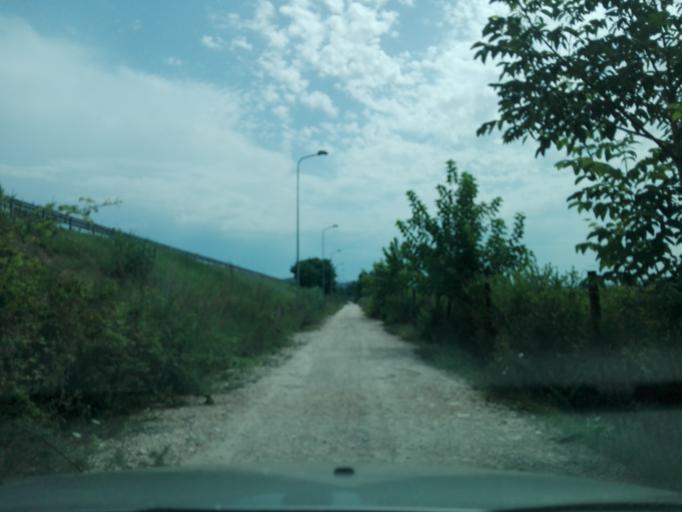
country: IT
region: Abruzzo
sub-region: Provincia di Pescara
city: Cappelle sul Tavo
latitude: 42.4935
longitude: 14.1133
